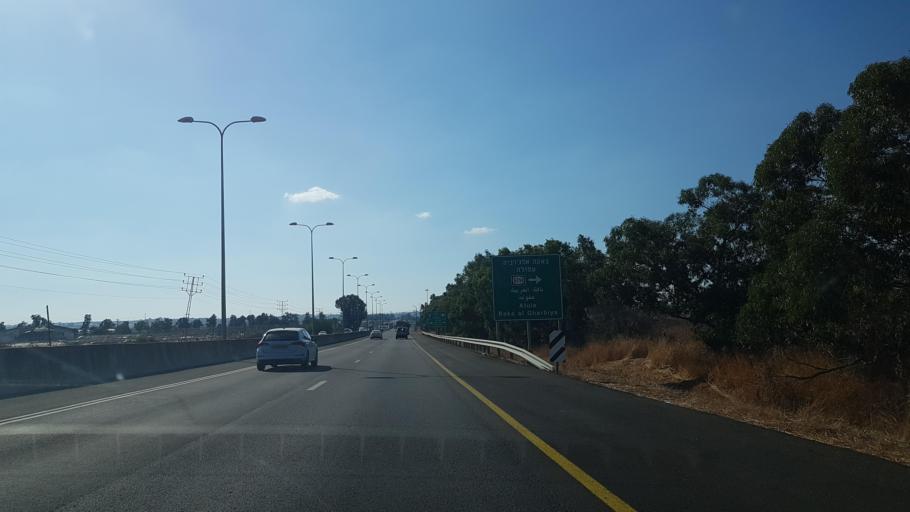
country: PS
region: West Bank
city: Tulkarm
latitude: 32.3119
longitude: 35.0046
